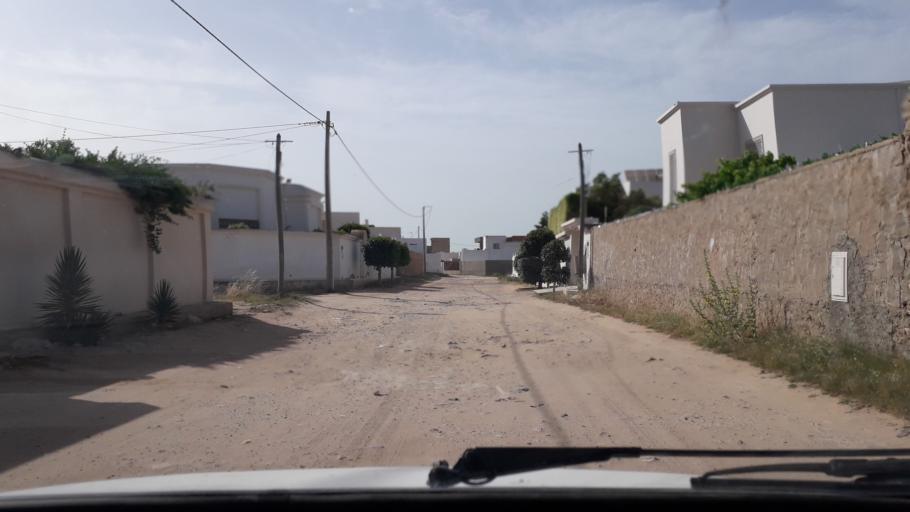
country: TN
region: Safaqis
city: Al Qarmadah
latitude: 34.8089
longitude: 10.7702
